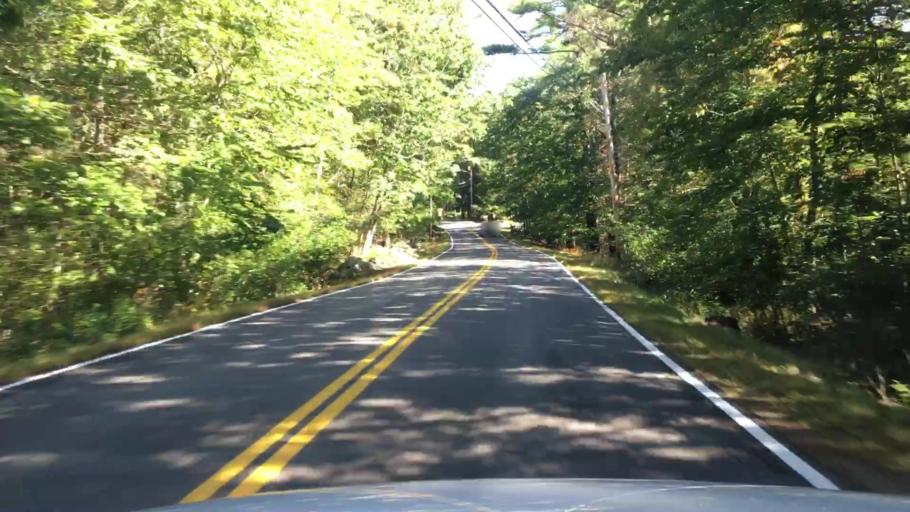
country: US
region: Maine
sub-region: York County
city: Kittery Point
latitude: 43.1063
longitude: -70.6744
